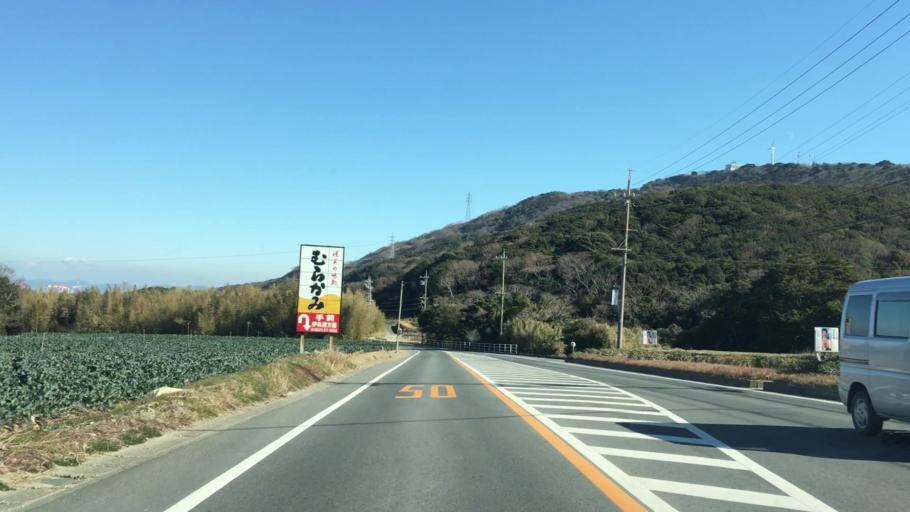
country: JP
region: Aichi
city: Tahara
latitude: 34.6863
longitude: 137.2468
